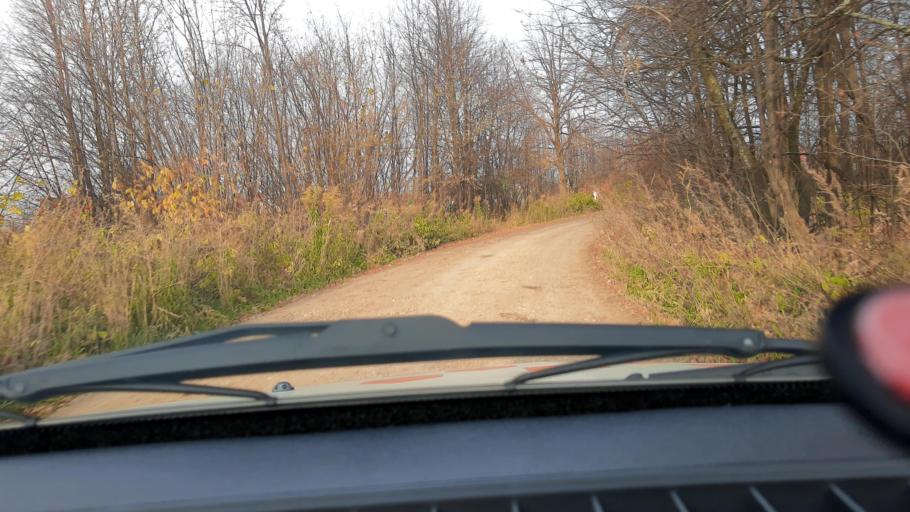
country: RU
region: Bashkortostan
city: Iglino
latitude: 54.7985
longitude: 56.3401
